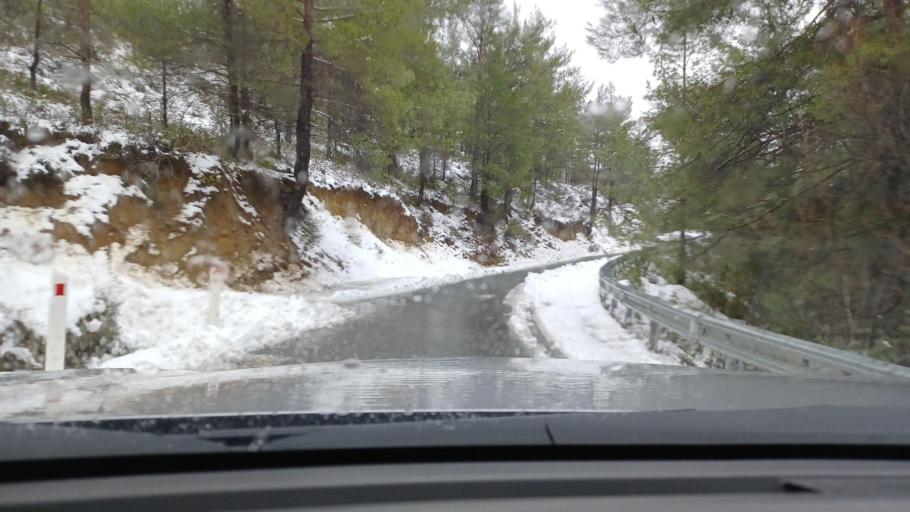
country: CY
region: Limassol
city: Pelendri
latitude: 34.9145
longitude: 32.9514
